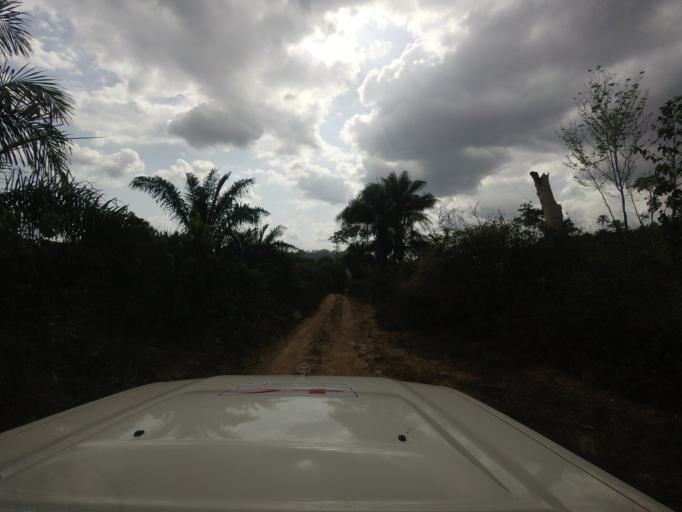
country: LR
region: Lofa
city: Voinjama
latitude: 8.3920
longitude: -9.6102
